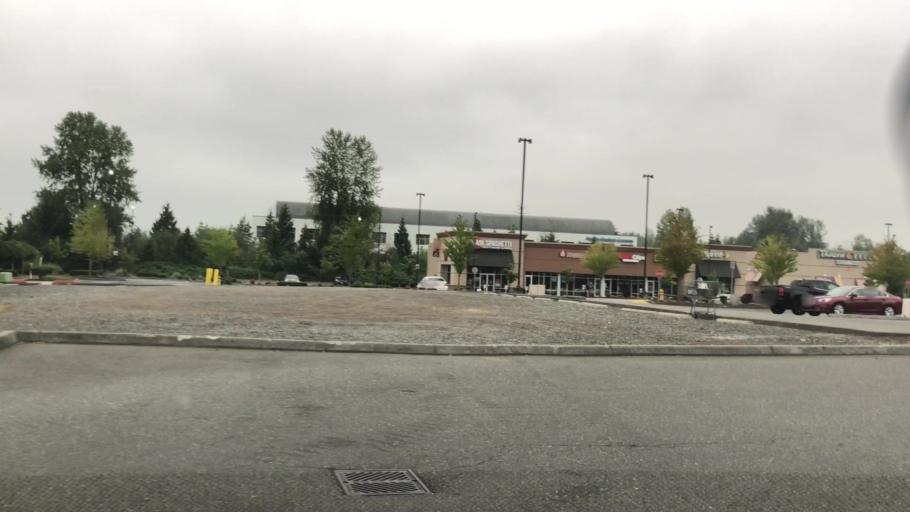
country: US
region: Washington
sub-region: Snohomish County
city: North Creek
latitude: 47.8062
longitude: -122.2064
